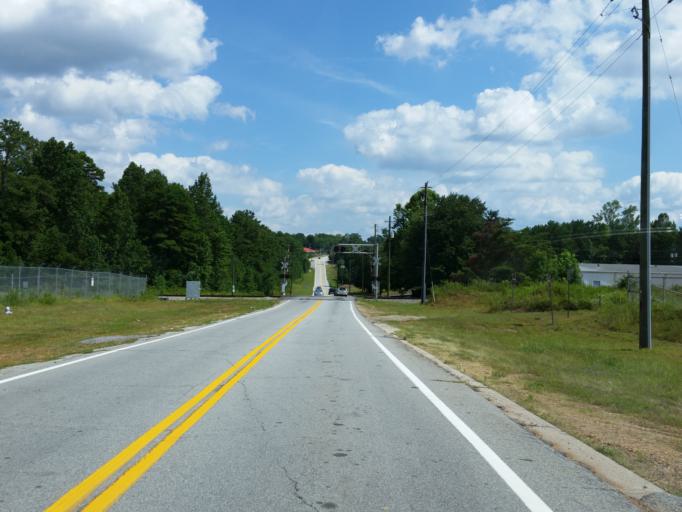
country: US
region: Georgia
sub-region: Gwinnett County
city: Lawrenceville
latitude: 33.9826
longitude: -83.9498
